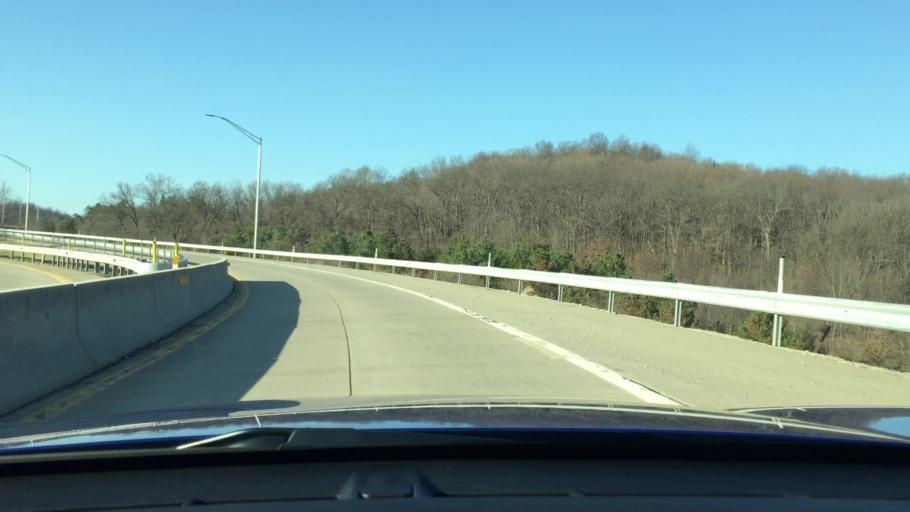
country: US
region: Pennsylvania
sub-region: Westmoreland County
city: New Stanton
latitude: 40.2350
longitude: -79.6001
